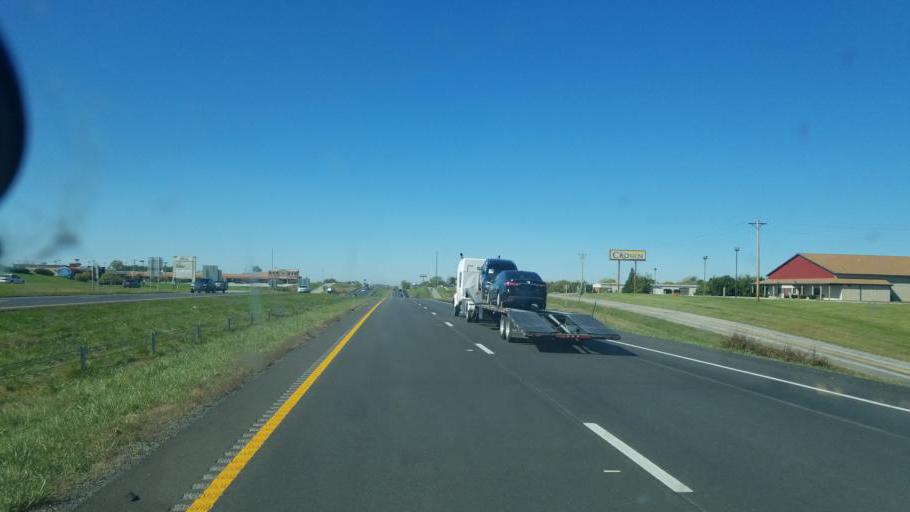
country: US
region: Missouri
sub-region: Lafayette County
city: Odessa
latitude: 39.0087
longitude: -93.9696
